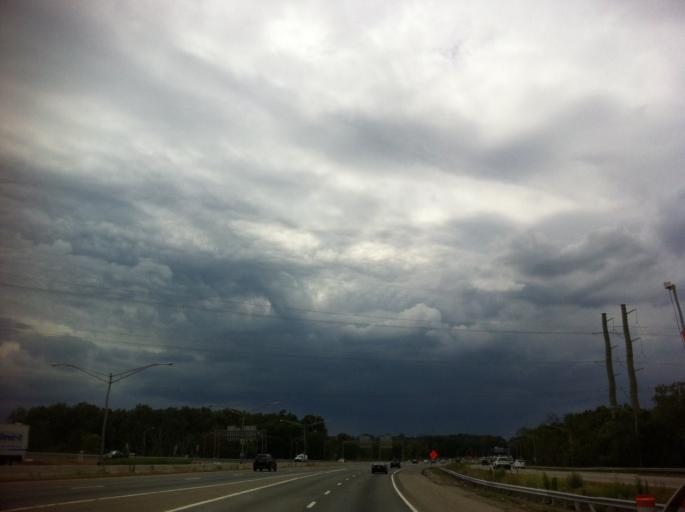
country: US
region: New Jersey
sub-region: Essex County
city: Fairfield
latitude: 40.8616
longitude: -74.3432
